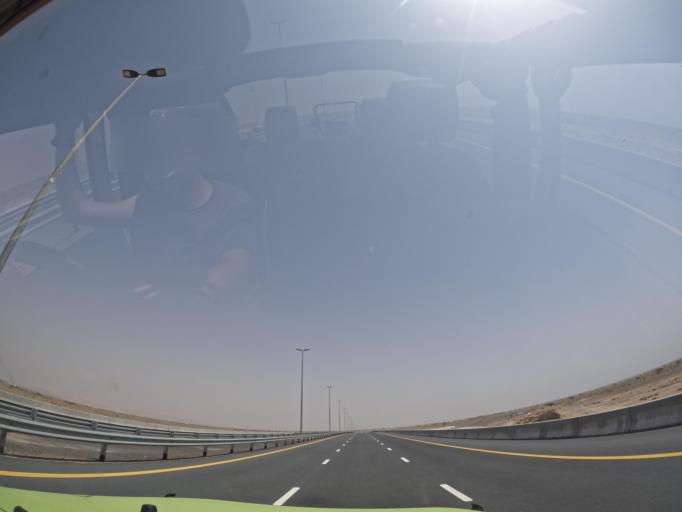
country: AE
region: Ash Shariqah
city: Adh Dhayd
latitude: 24.9877
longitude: 55.8592
